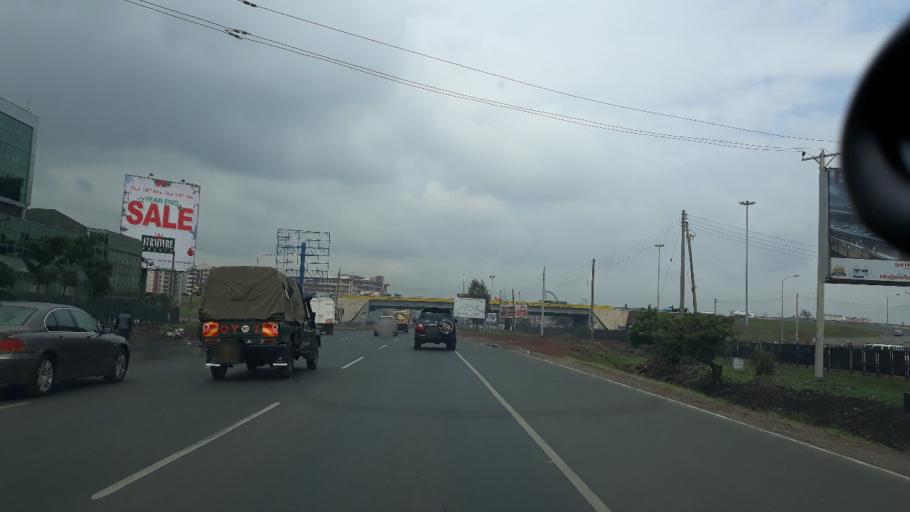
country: KE
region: Nairobi Area
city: Pumwani
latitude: -1.3261
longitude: 36.8490
